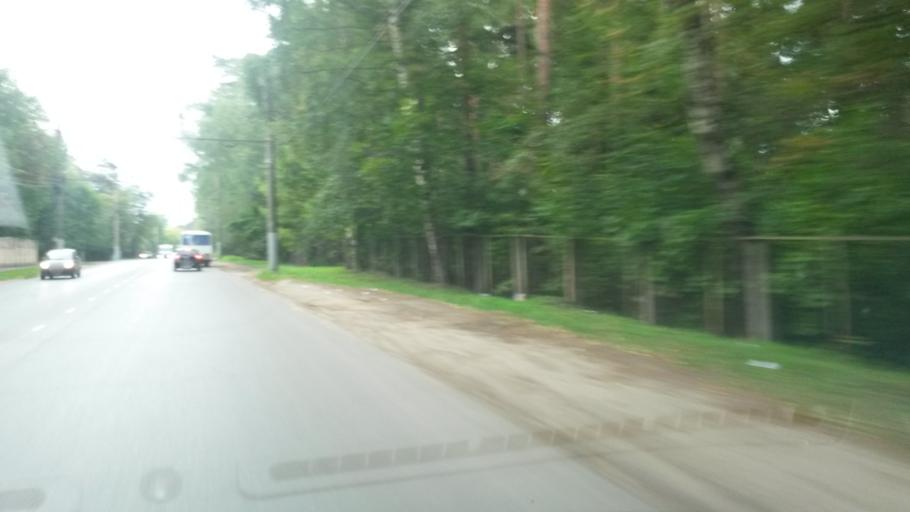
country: RU
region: Ivanovo
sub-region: Gorod Ivanovo
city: Ivanovo
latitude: 57.0250
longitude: 40.9408
